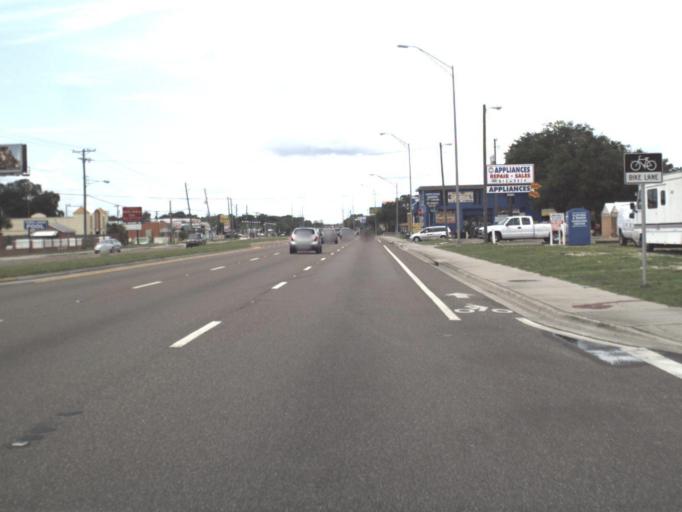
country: US
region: Florida
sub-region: Hillsborough County
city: Egypt Lake-Leto
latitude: 27.9963
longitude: -82.4927
